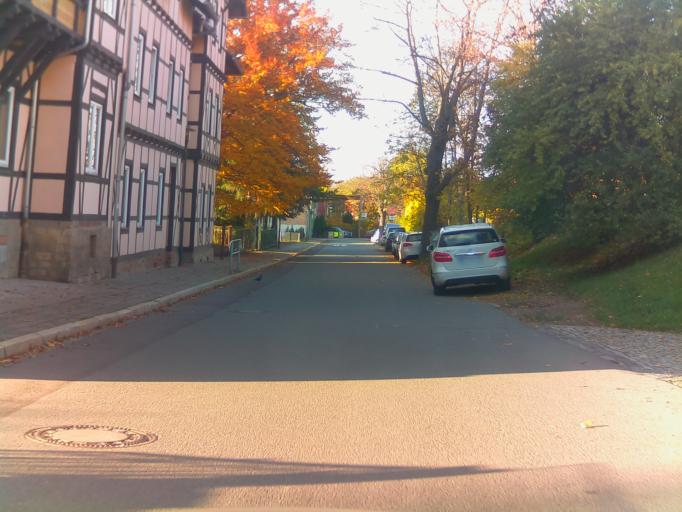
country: DE
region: Thuringia
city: Arnstadt
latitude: 50.8295
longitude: 10.9567
